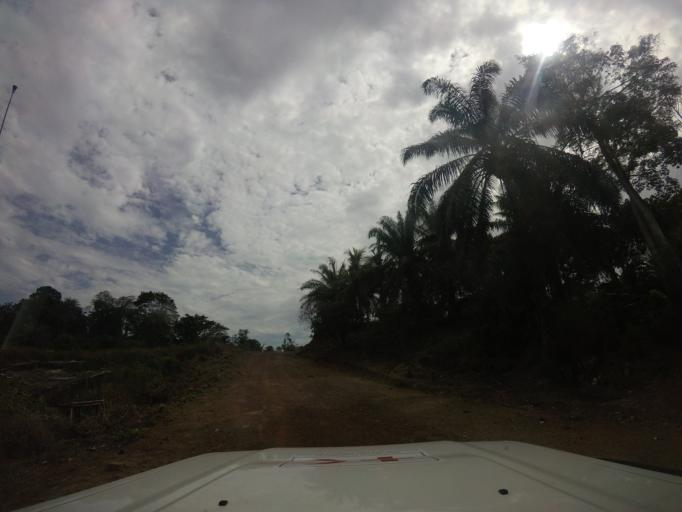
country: SL
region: Southern Province
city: Zimmi
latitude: 7.1642
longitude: -11.2424
